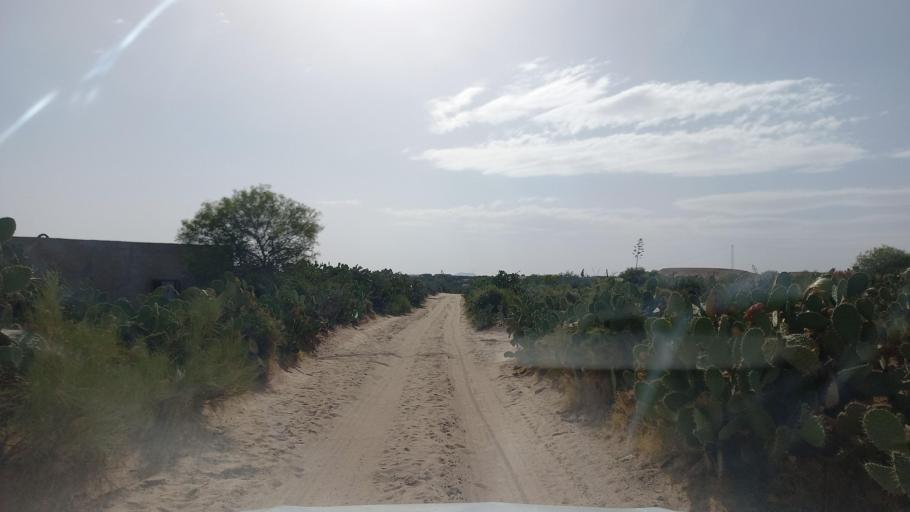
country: TN
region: Al Qasrayn
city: Kasserine
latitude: 35.2753
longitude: 8.9428
